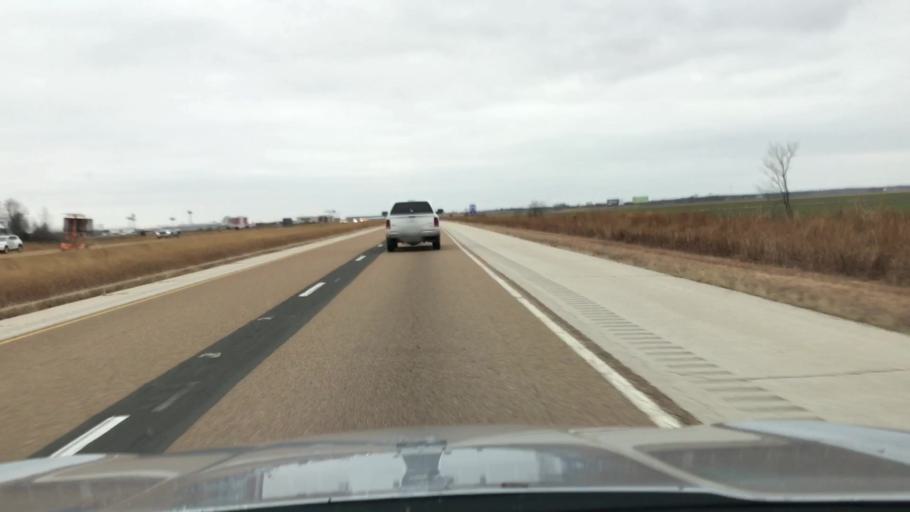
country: US
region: Illinois
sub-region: Montgomery County
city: Litchfield
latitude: 39.1891
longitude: -89.6719
